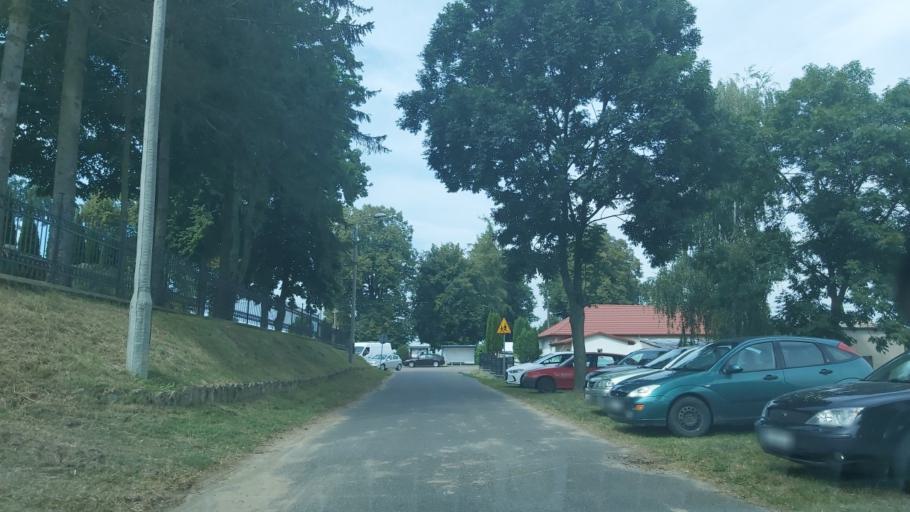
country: PL
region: Kujawsko-Pomorskie
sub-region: Powiat golubsko-dobrzynski
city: Zbojno
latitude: 53.0318
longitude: 19.1699
